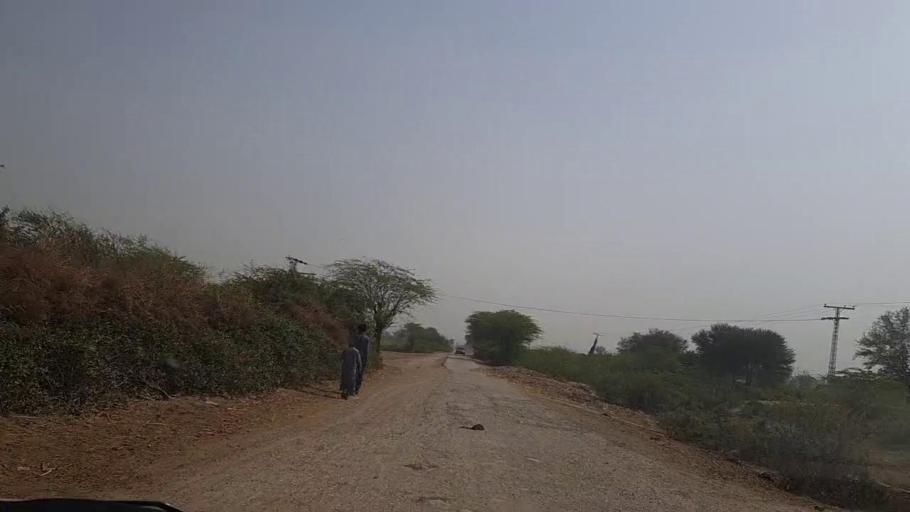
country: PK
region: Sindh
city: Pithoro
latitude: 25.4815
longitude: 69.2197
